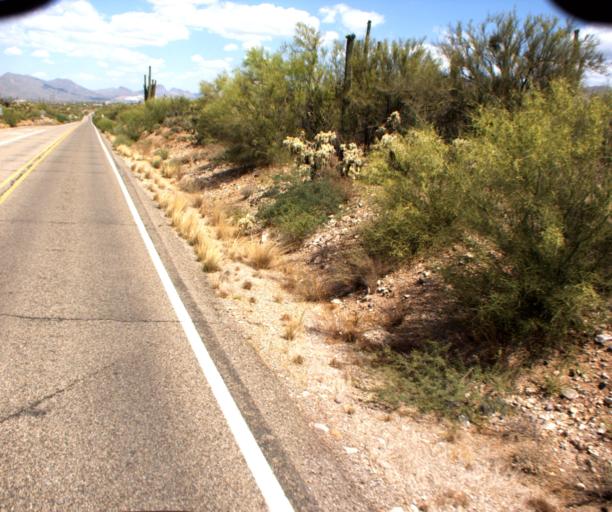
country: US
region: Arizona
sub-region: Pinal County
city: Kearny
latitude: 33.0661
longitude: -110.9117
